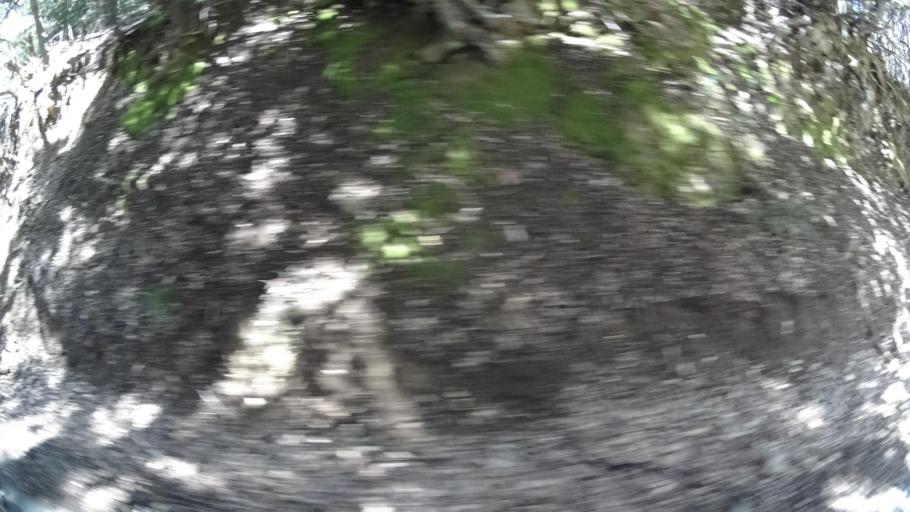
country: US
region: California
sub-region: Humboldt County
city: Rio Dell
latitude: 40.2761
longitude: -124.0717
